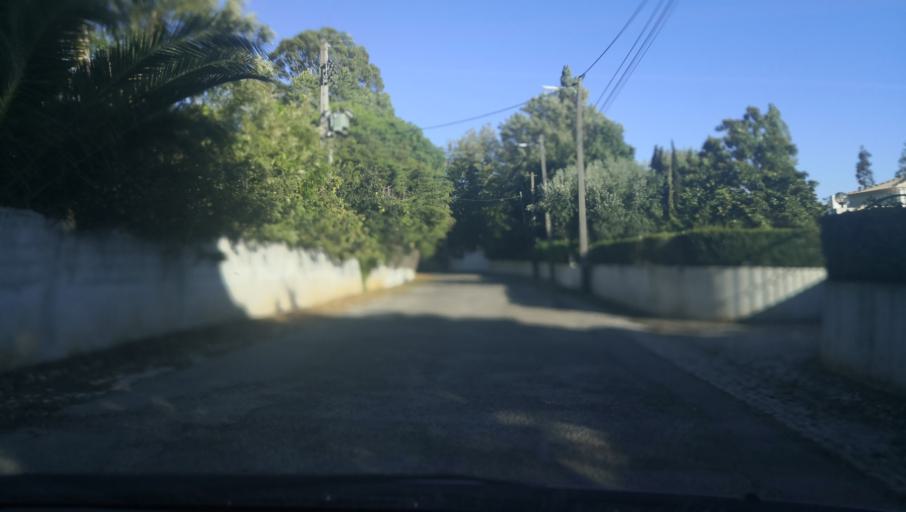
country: PT
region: Setubal
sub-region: Palmela
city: Palmela
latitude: 38.5524
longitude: -8.8889
